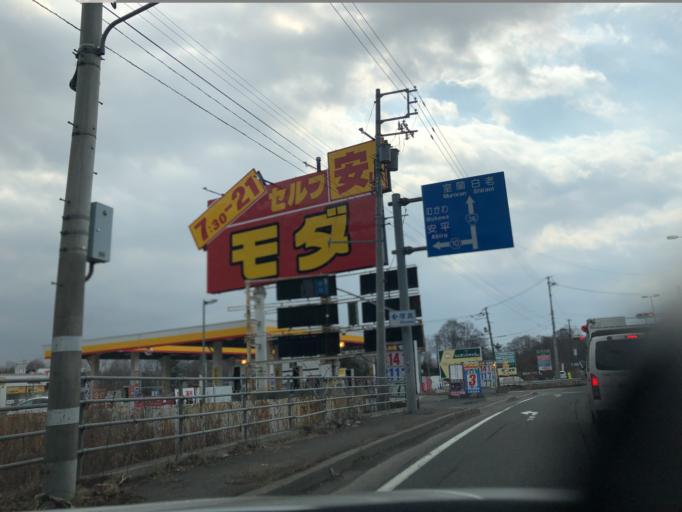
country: JP
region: Hokkaido
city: Chitose
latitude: 42.7679
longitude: 141.7092
